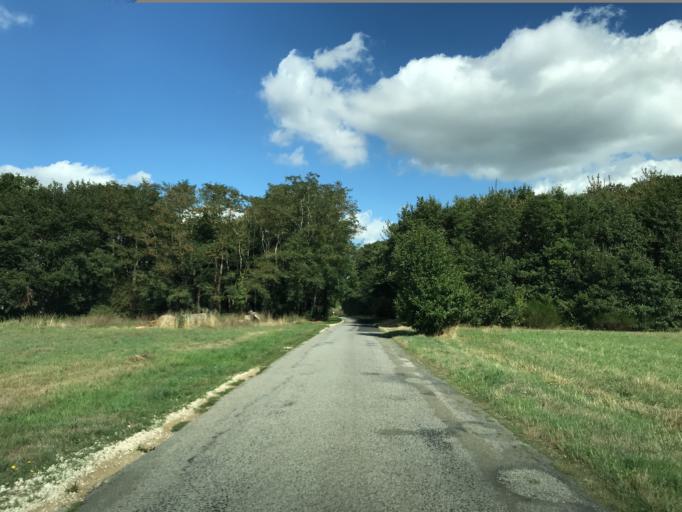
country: FR
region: Haute-Normandie
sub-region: Departement de l'Eure
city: La Chapelle-Reanville
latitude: 49.0996
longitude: 1.3901
